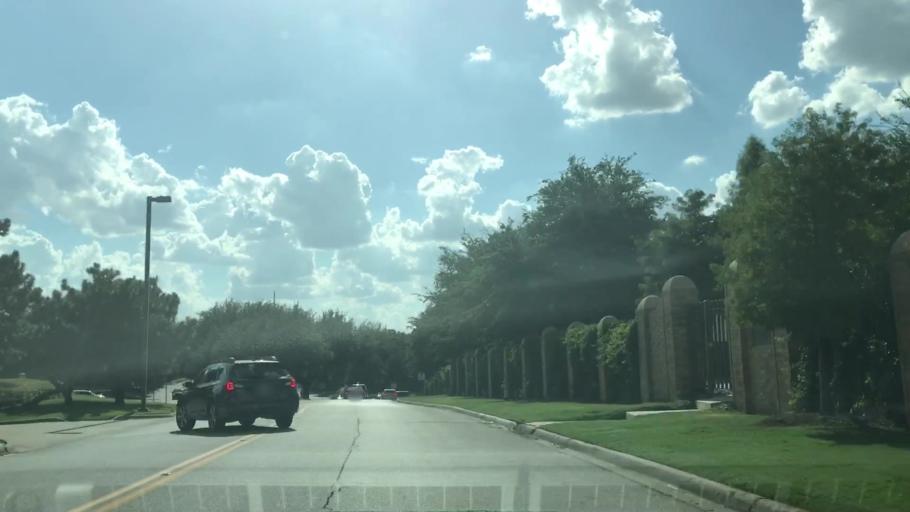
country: US
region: Texas
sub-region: Dallas County
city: Irving
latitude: 32.8618
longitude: -96.9584
